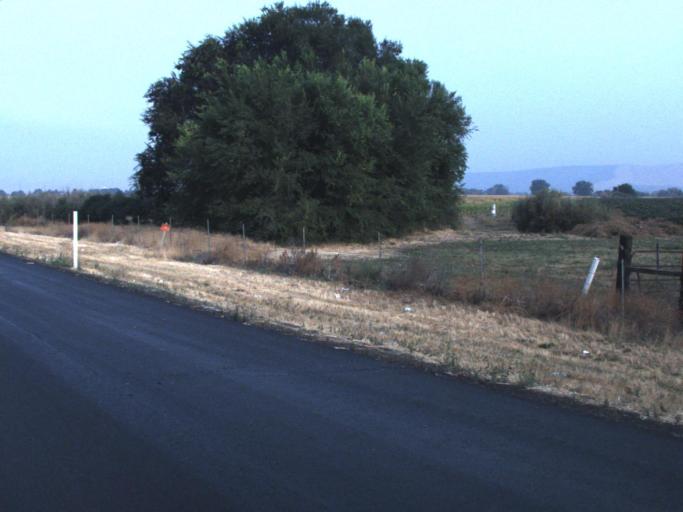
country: US
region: Washington
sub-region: Yakima County
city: Wapato
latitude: 46.4212
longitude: -120.4017
